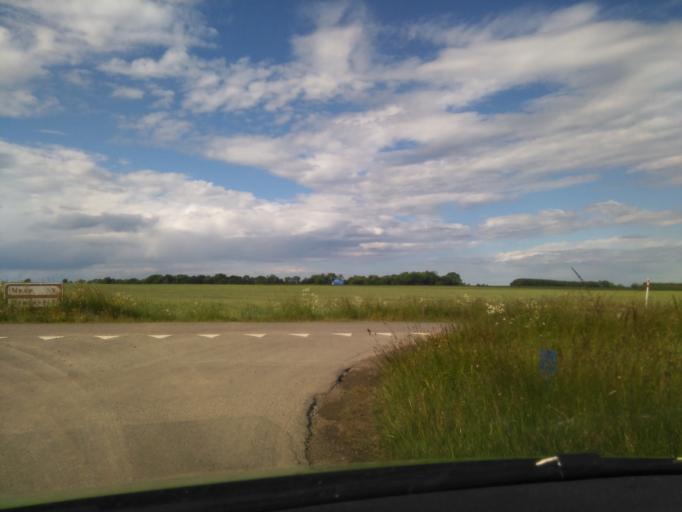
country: DK
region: Capital Region
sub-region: Bornholm Kommune
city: Nexo
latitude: 55.1242
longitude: 15.0803
